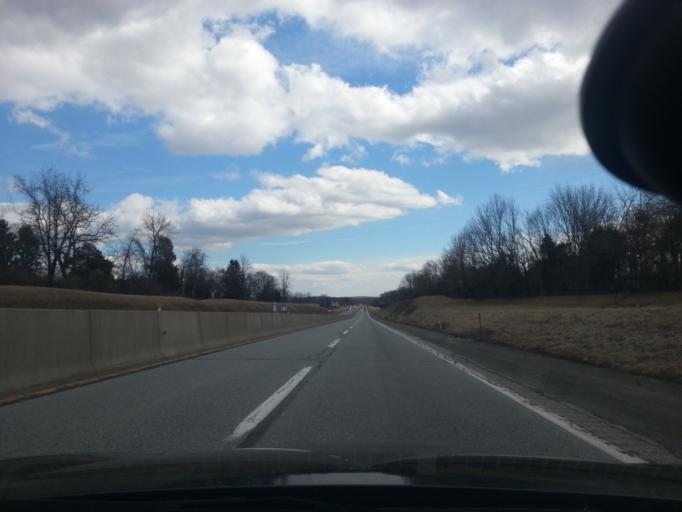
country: US
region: Pennsylvania
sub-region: Bucks County
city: Spinnerstown
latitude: 40.4536
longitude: -75.4390
